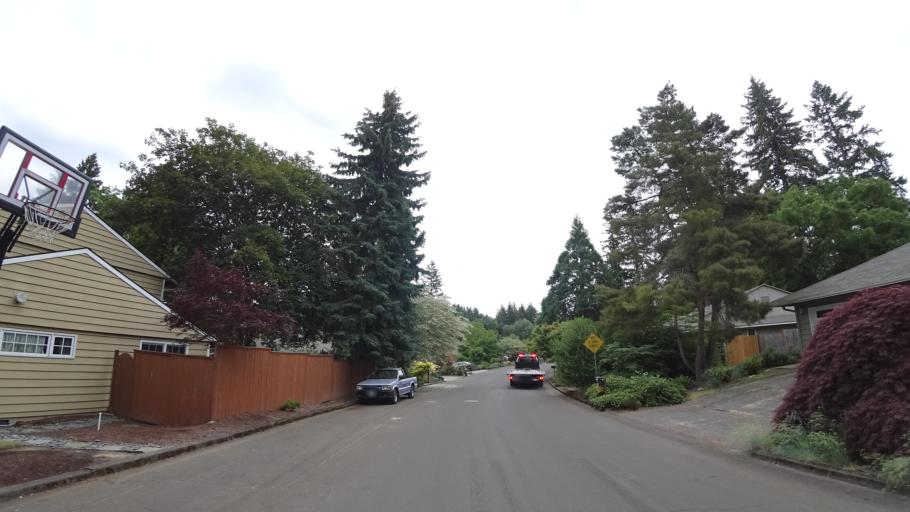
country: US
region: Oregon
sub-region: Washington County
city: Garden Home-Whitford
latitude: 45.4601
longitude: -122.7675
